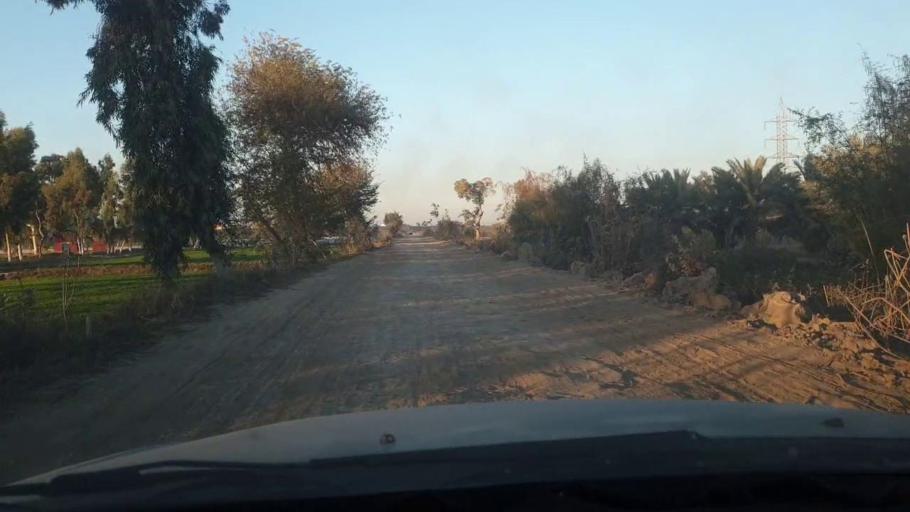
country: PK
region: Sindh
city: Ghotki
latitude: 28.0396
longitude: 69.3243
